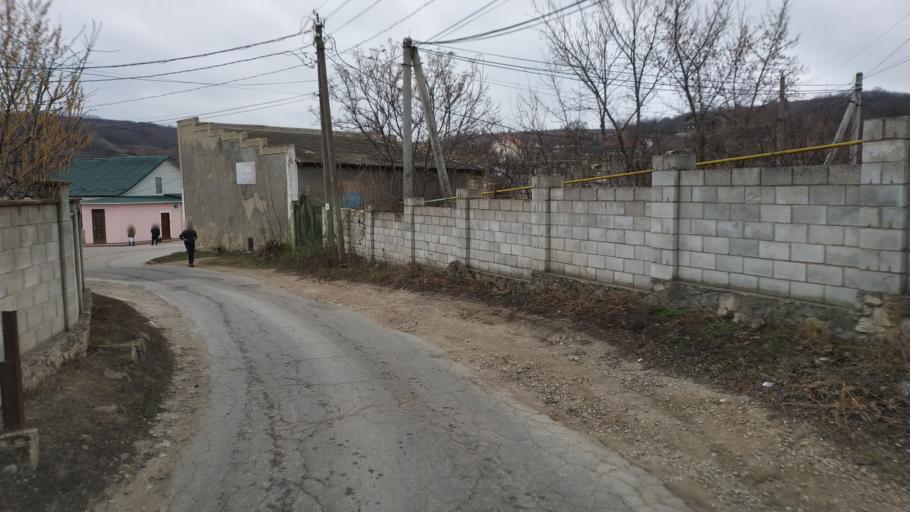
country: MD
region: Laloveni
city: Ialoveni
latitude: 46.9007
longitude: 28.8039
